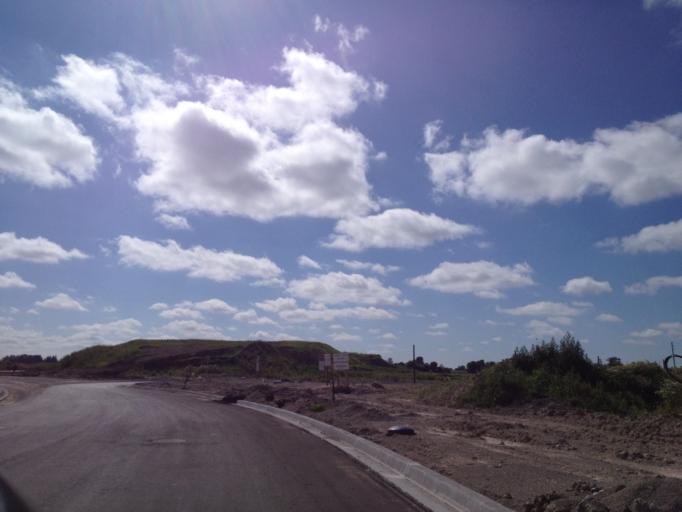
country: CA
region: Ontario
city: London
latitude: 43.0236
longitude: -81.3319
